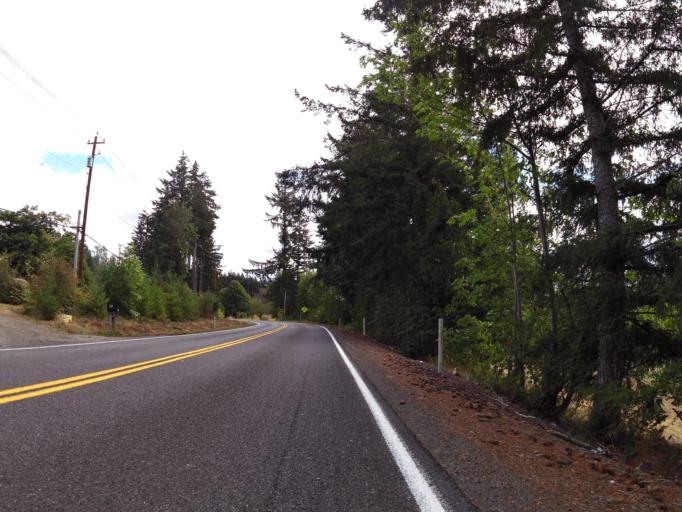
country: US
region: Washington
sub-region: Mason County
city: Shelton
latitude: 47.1799
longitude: -123.0903
